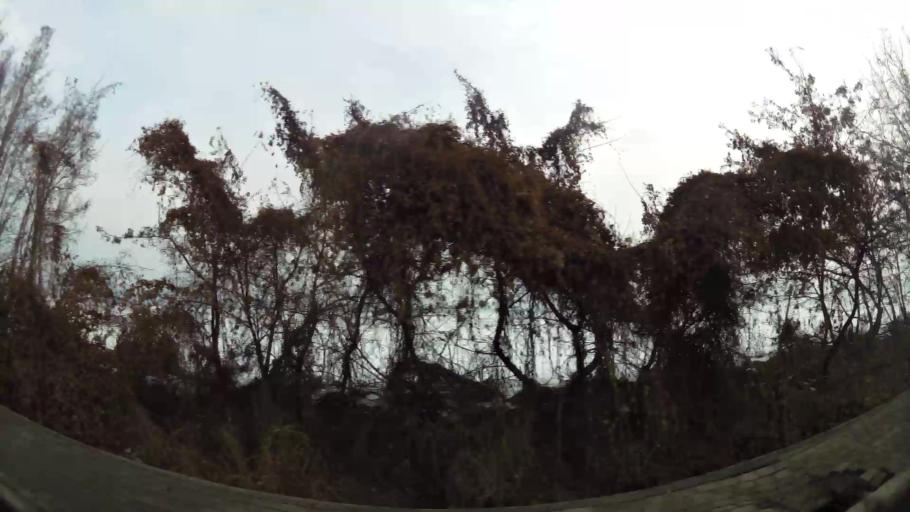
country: MK
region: Kisela Voda
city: Kisela Voda
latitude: 41.9879
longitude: 21.5155
